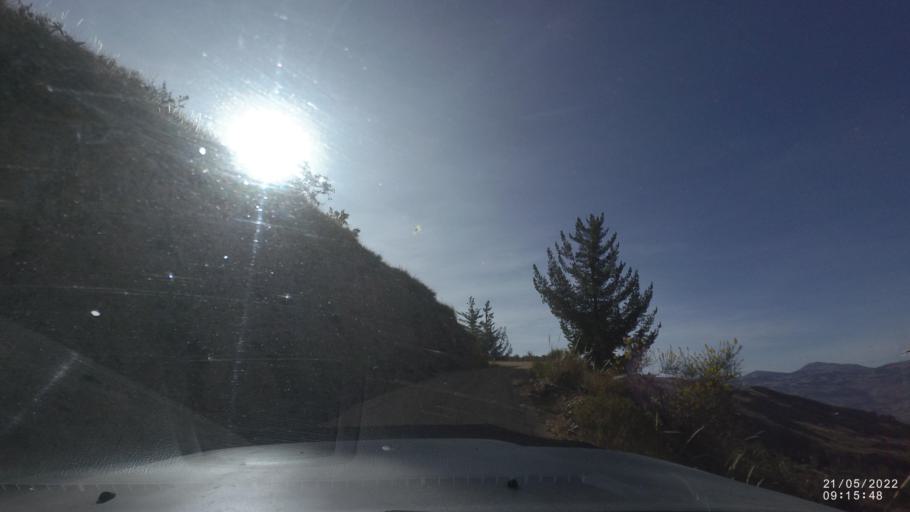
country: BO
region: Cochabamba
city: Cochabamba
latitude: -17.3642
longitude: -66.0262
